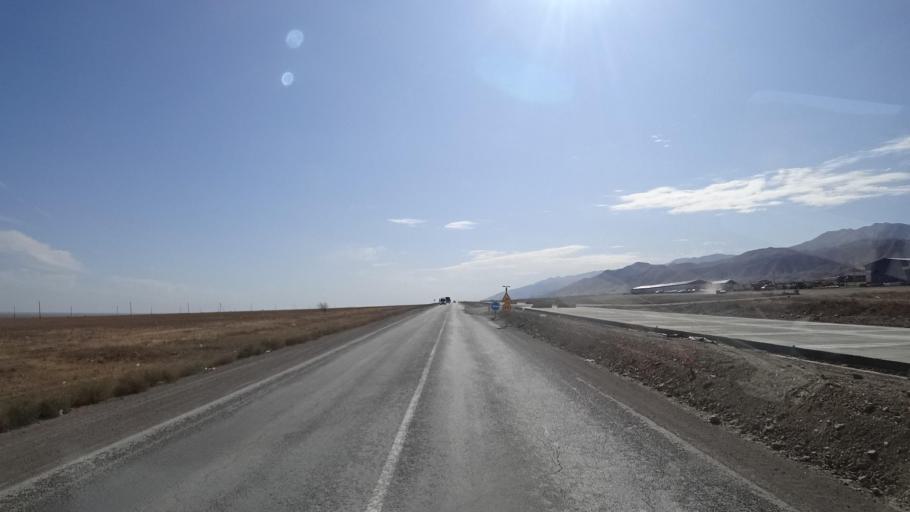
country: KG
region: Chuy
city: Ivanovka
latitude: 43.3909
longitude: 75.1405
